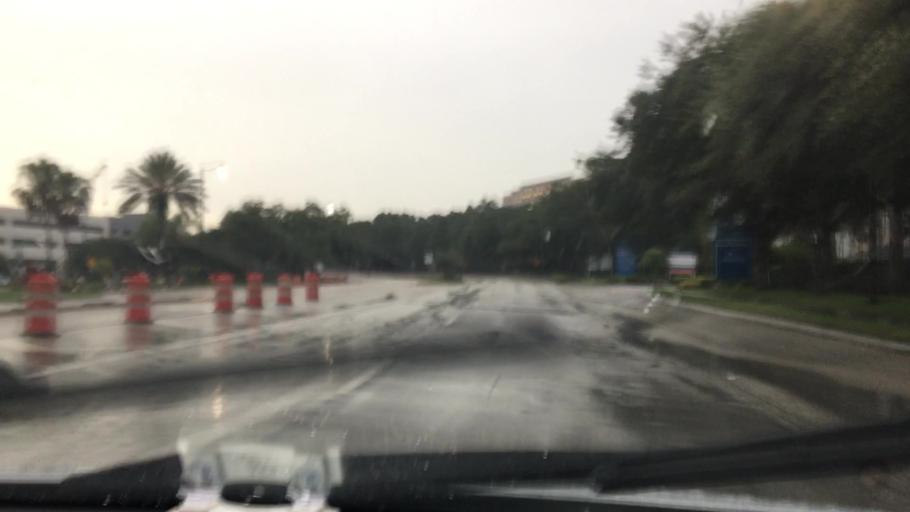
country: US
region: Florida
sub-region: Seminole County
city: Altamonte Springs
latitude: 28.6709
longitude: -81.3850
